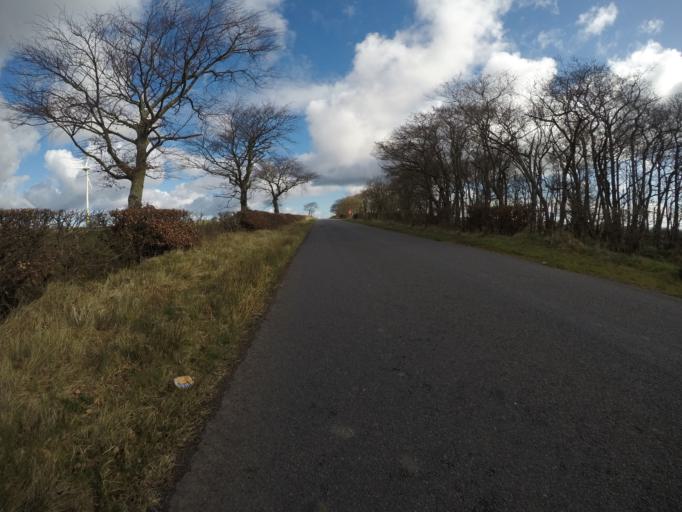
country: GB
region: Scotland
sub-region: North Ayrshire
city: Kilwinning
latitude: 55.6784
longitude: -4.6548
